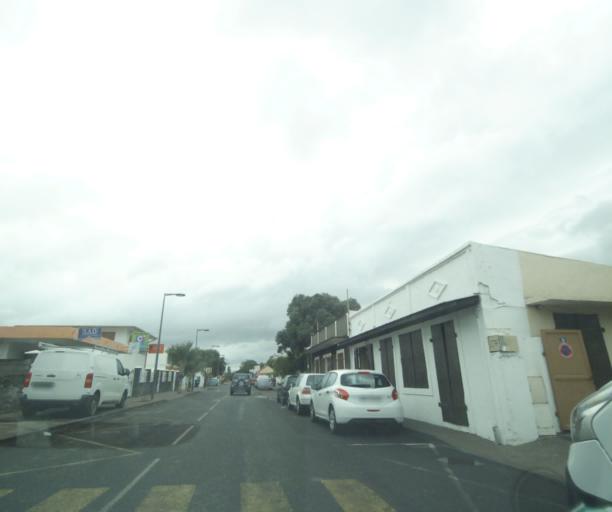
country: RE
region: Reunion
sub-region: Reunion
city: Saint-Paul
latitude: -21.0073
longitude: 55.2757
